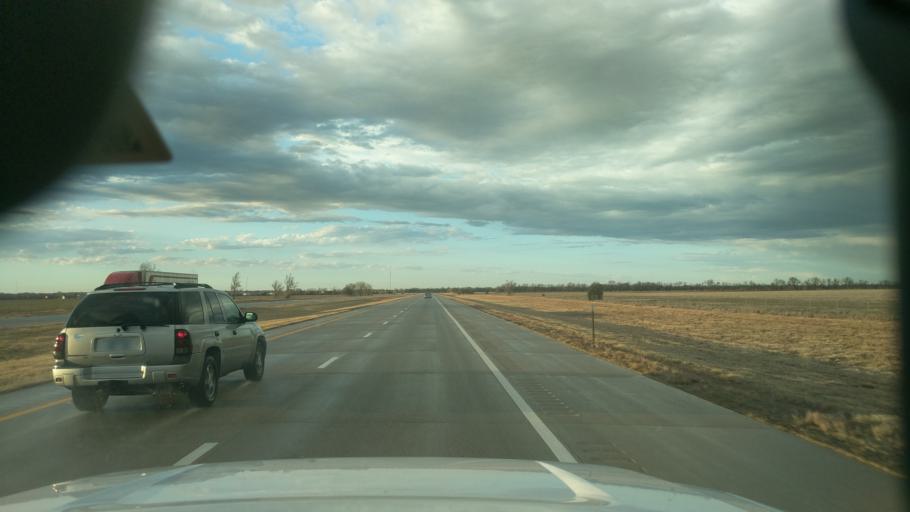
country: US
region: Kansas
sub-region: Harvey County
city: Hesston
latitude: 38.1230
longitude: -97.3952
